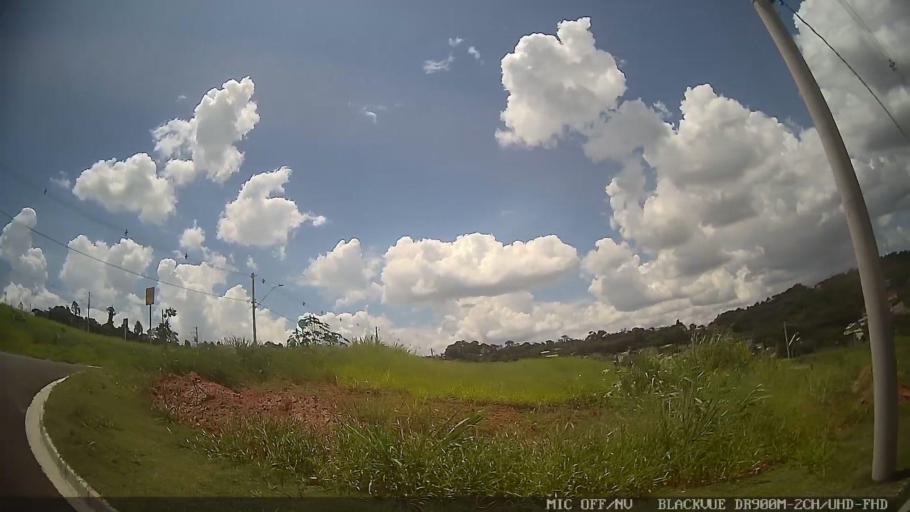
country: BR
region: Sao Paulo
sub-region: Atibaia
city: Atibaia
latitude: -23.1249
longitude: -46.6016
